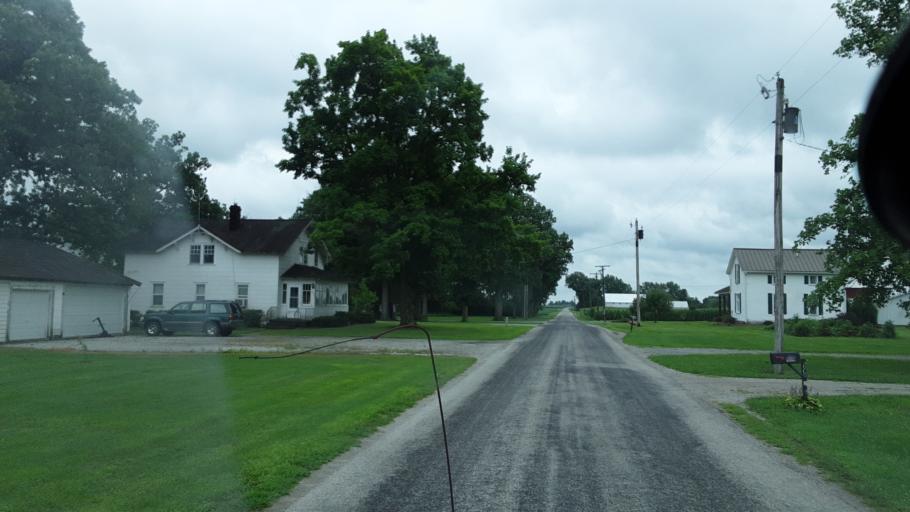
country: US
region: Indiana
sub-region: Wells County
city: Ossian
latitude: 40.8104
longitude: -85.0718
